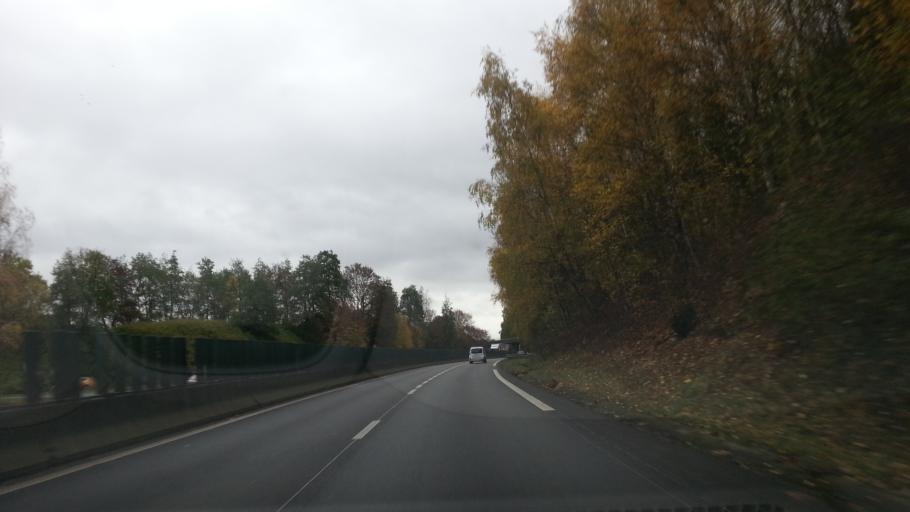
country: FR
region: Picardie
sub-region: Departement de l'Oise
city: Creil
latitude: 49.2572
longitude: 2.4923
